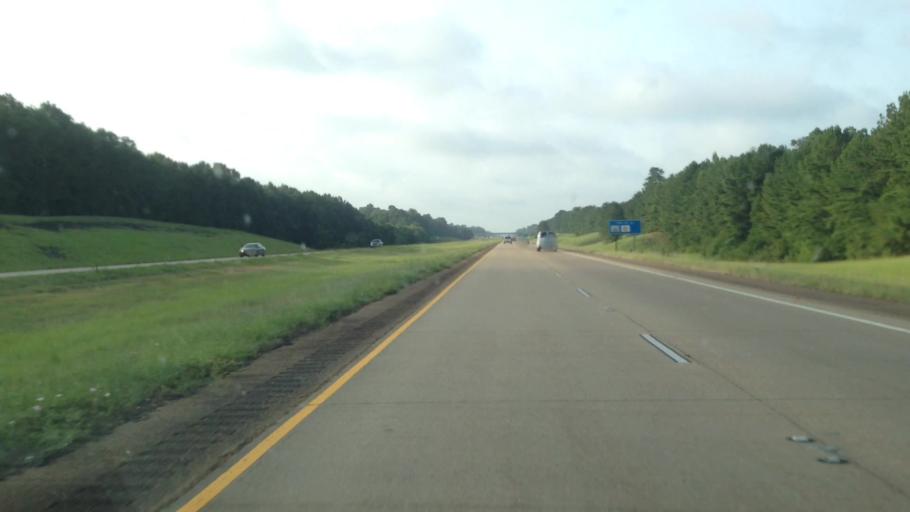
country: US
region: Louisiana
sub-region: Rapides Parish
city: Lecompte
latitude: 31.0857
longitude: -92.4419
